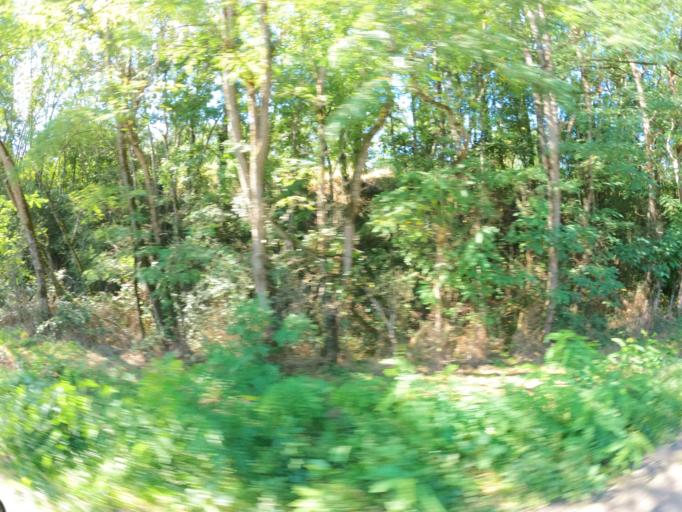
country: FR
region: Poitou-Charentes
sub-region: Departement de la Vienne
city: Lathus-Saint-Remy
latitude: 46.3673
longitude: 0.9372
